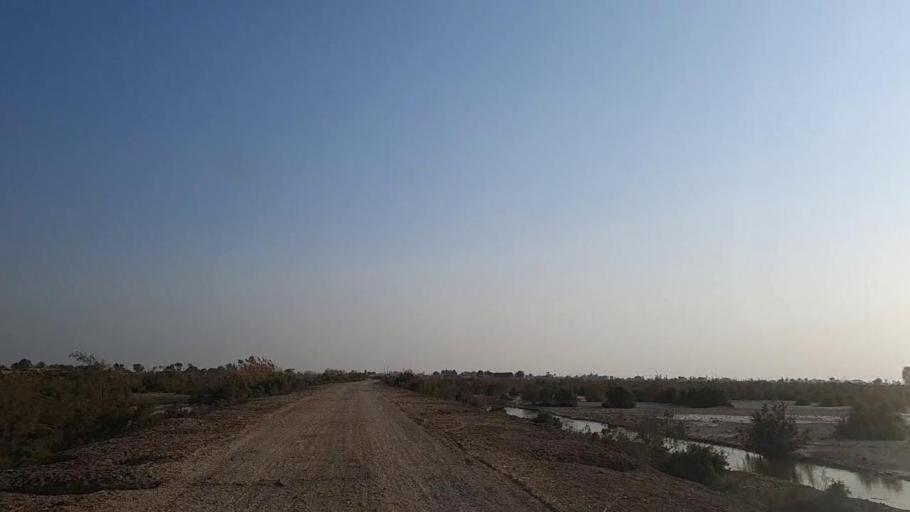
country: PK
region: Sindh
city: Daur
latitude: 26.4252
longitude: 68.3540
